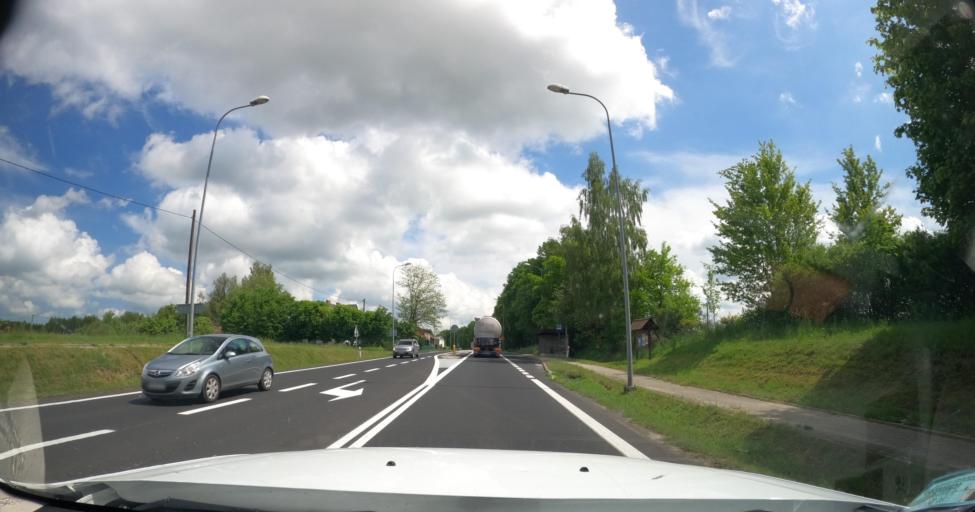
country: PL
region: Pomeranian Voivodeship
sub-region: Powiat slupski
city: Kobylnica
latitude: 54.4338
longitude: 16.9047
